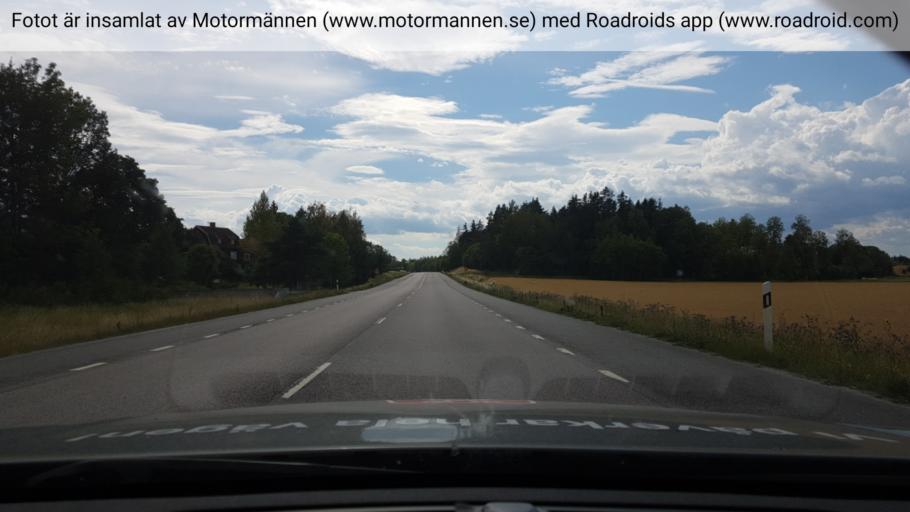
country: SE
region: Uppsala
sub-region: Uppsala Kommun
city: Uppsala
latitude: 59.8428
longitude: 17.5404
